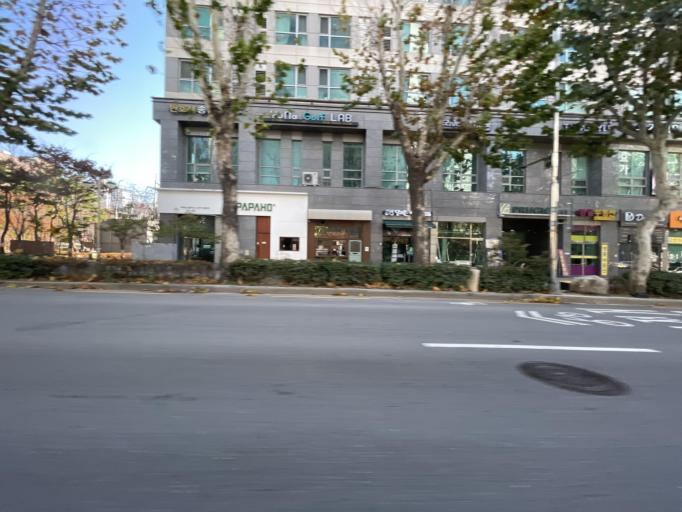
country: KR
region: Seoul
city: Seoul
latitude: 37.5481
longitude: 126.9542
